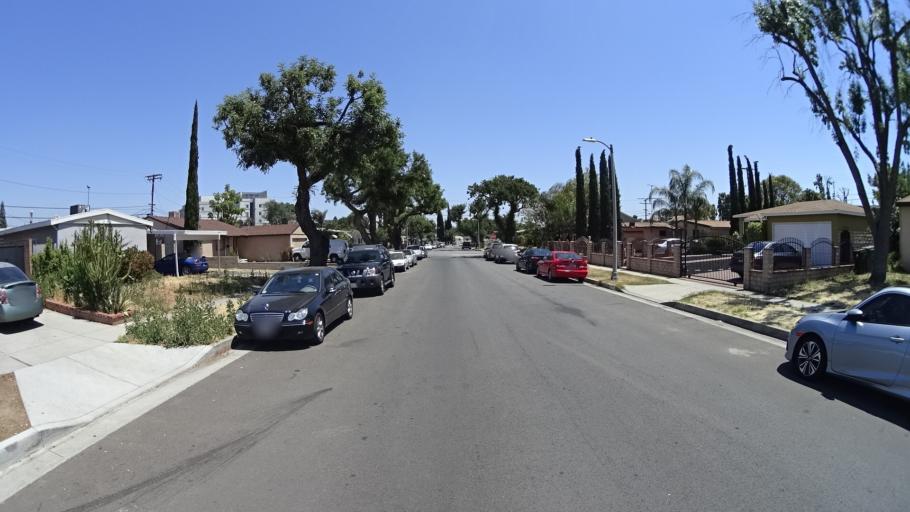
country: US
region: California
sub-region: Los Angeles County
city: Van Nuys
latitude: 34.2193
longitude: -118.4334
